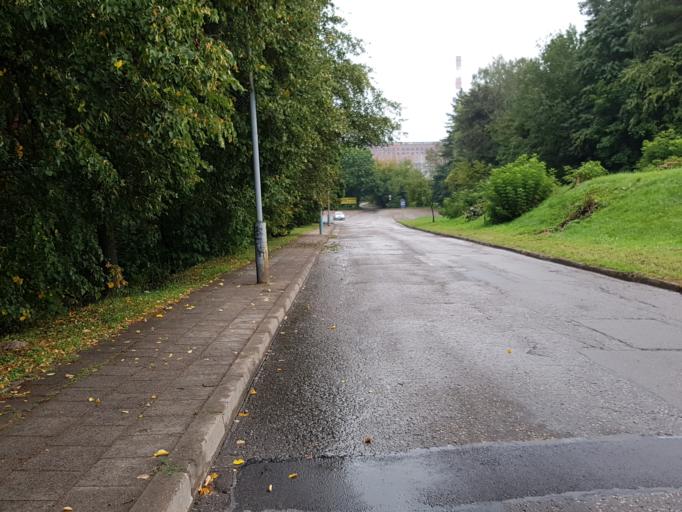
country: LT
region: Vilnius County
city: Lazdynai
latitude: 54.6672
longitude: 25.2193
